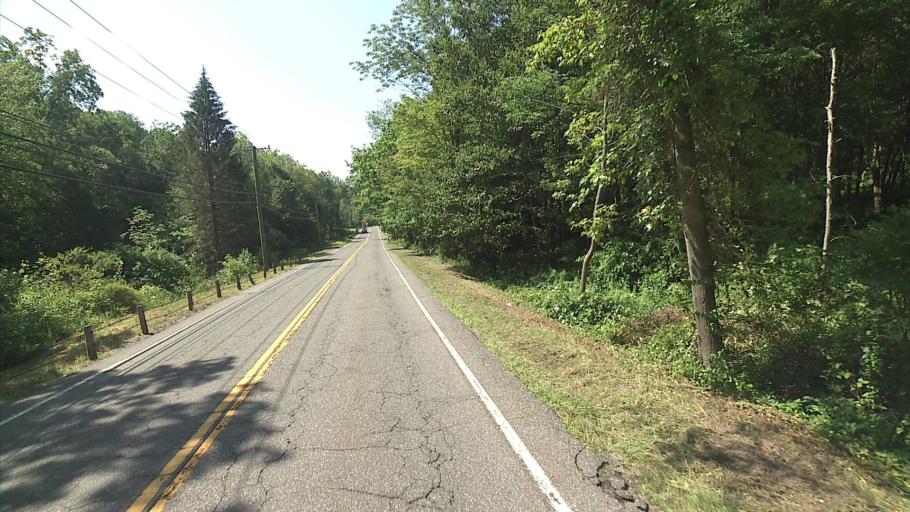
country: US
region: Connecticut
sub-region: Litchfield County
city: New Preston
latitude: 41.7118
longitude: -73.3453
